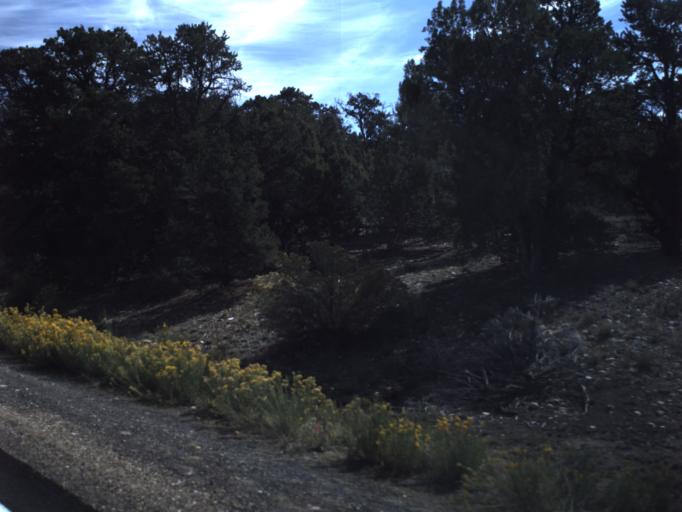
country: US
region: Utah
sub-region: Garfield County
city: Panguitch
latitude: 37.6207
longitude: -111.8714
